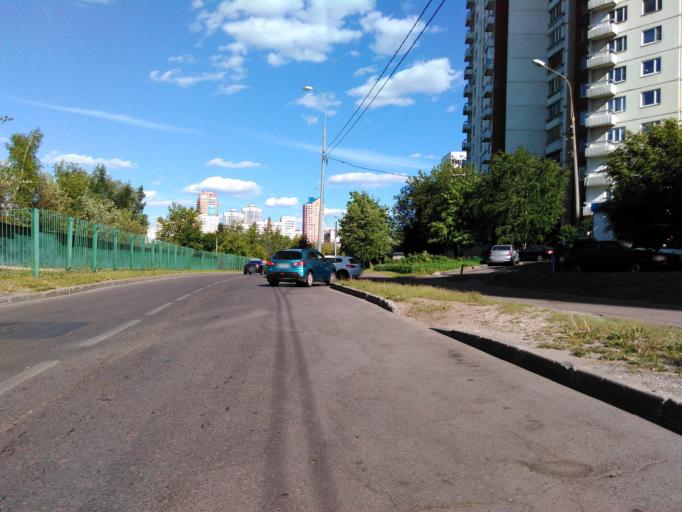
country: RU
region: Moscow
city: Troparevo
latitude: 55.6675
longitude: 37.4959
